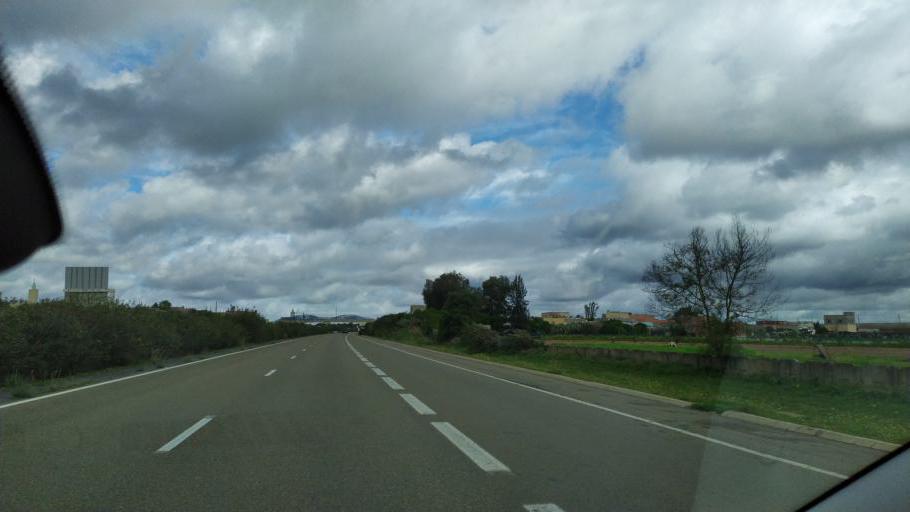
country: MA
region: Gharb-Chrarda-Beni Hssen
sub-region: Kenitra Province
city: Lalla Mimouna
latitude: 34.8610
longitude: -6.2214
